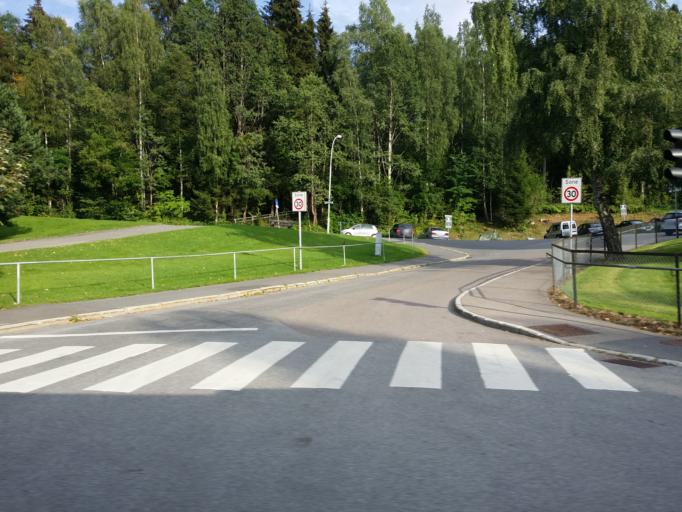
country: NO
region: Akershus
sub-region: Oppegard
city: Kolbotn
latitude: 59.8886
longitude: 10.8524
